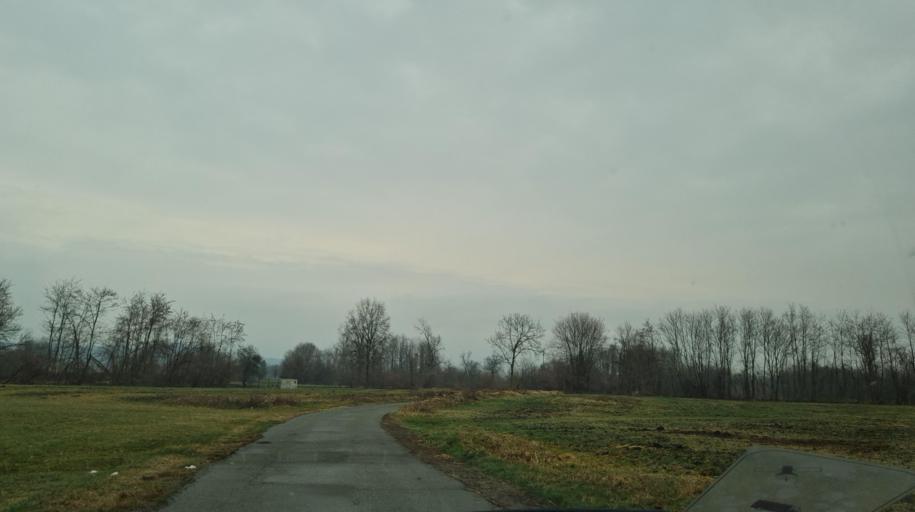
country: IT
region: Piedmont
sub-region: Provincia di Biella
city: Ceresane-Curanuova
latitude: 45.5157
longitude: 8.0195
